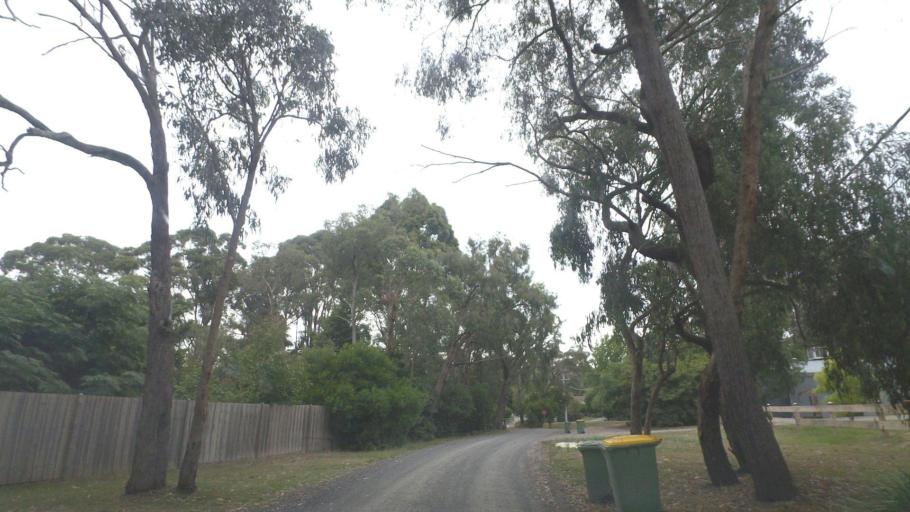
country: AU
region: Victoria
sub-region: Yarra Ranges
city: Mount Evelyn
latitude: -37.7604
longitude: 145.3988
